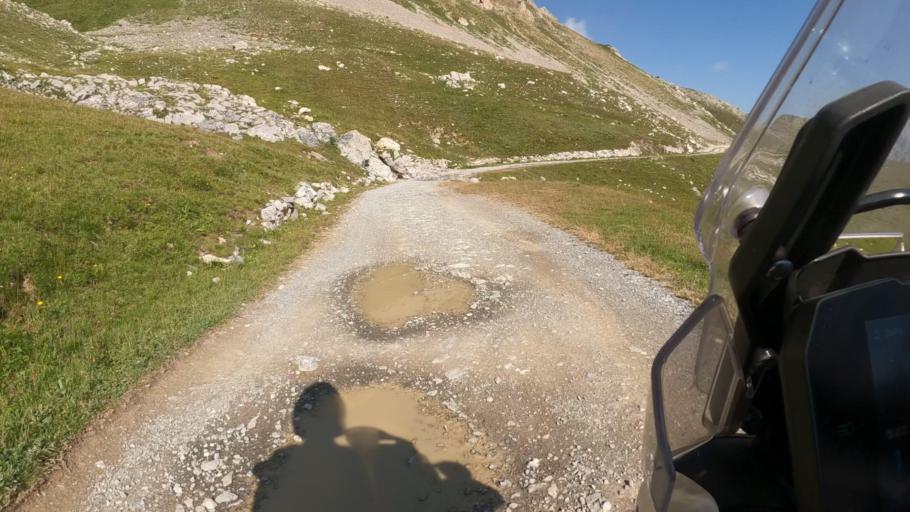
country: IT
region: Piedmont
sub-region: Provincia di Cuneo
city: Pietraporzio
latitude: 44.3862
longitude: 7.0292
